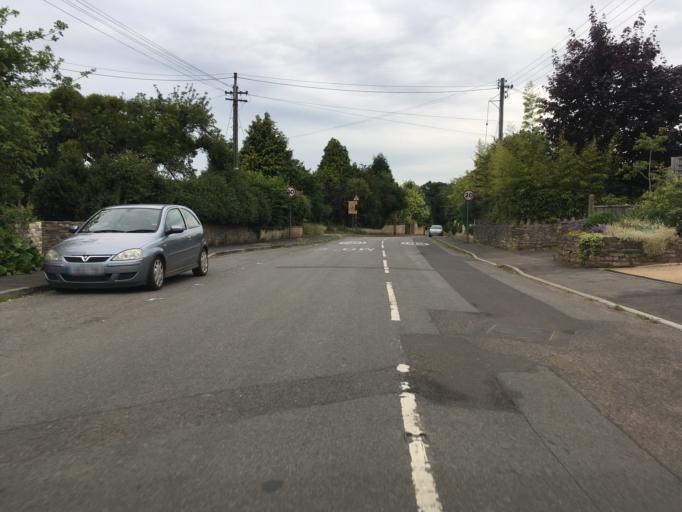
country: GB
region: England
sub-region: North Somerset
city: Long Ashton
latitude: 51.4219
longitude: -2.7055
